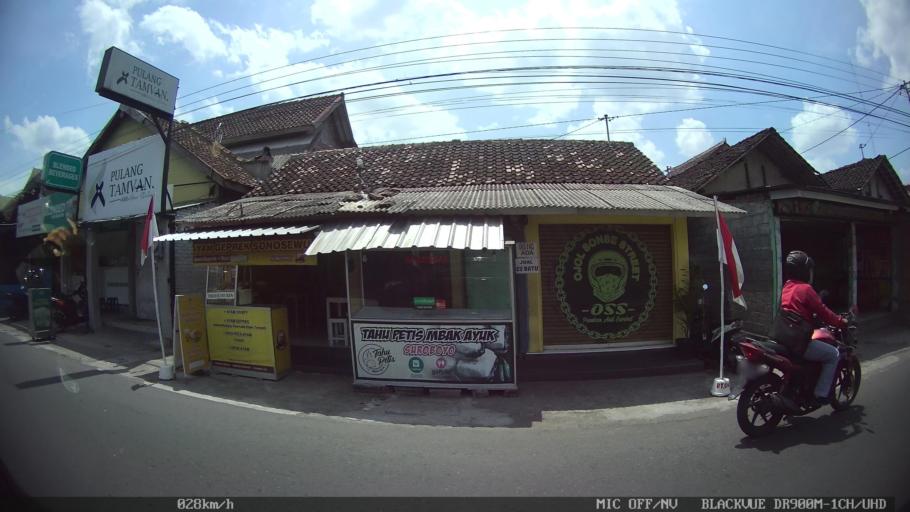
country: ID
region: Daerah Istimewa Yogyakarta
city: Gamping Lor
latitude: -7.8068
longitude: 110.3425
